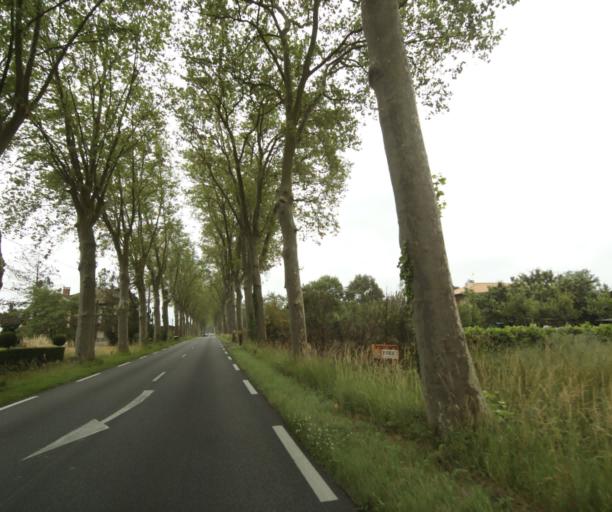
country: FR
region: Midi-Pyrenees
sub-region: Departement du Tarn-et-Garonne
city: Montbeton
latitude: 43.9946
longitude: 1.3146
